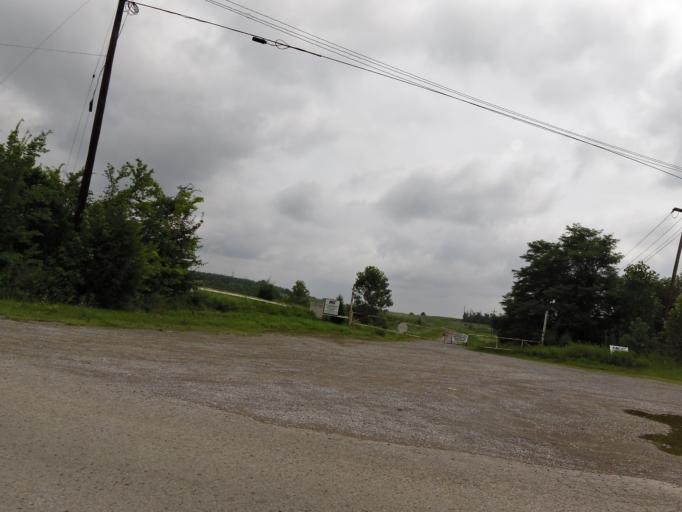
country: US
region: Kentucky
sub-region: Hopkins County
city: Madisonville
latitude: 37.3183
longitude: -87.3697
